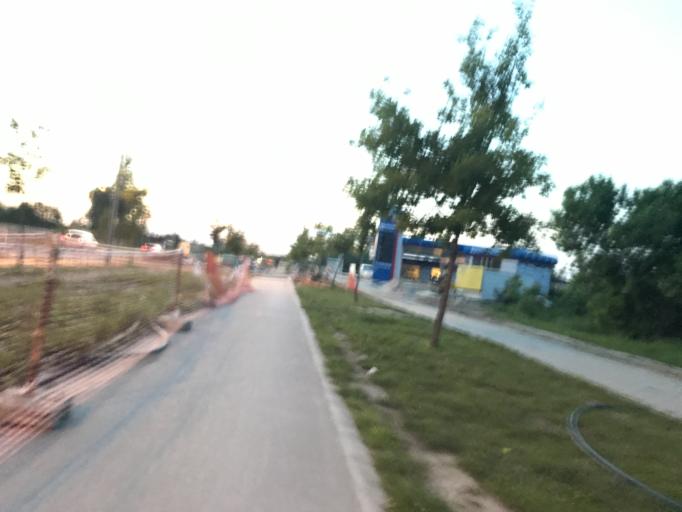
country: RS
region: Autonomna Pokrajina Vojvodina
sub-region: Juznobacki Okrug
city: Novi Sad
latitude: 45.2682
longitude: 19.8035
